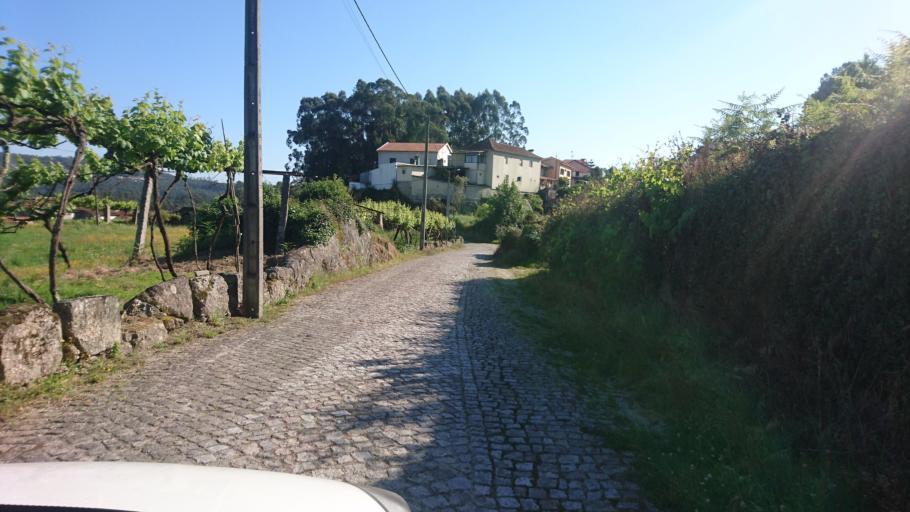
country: PT
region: Porto
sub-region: Paredes
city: Baltar
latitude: 41.1667
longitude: -8.3747
